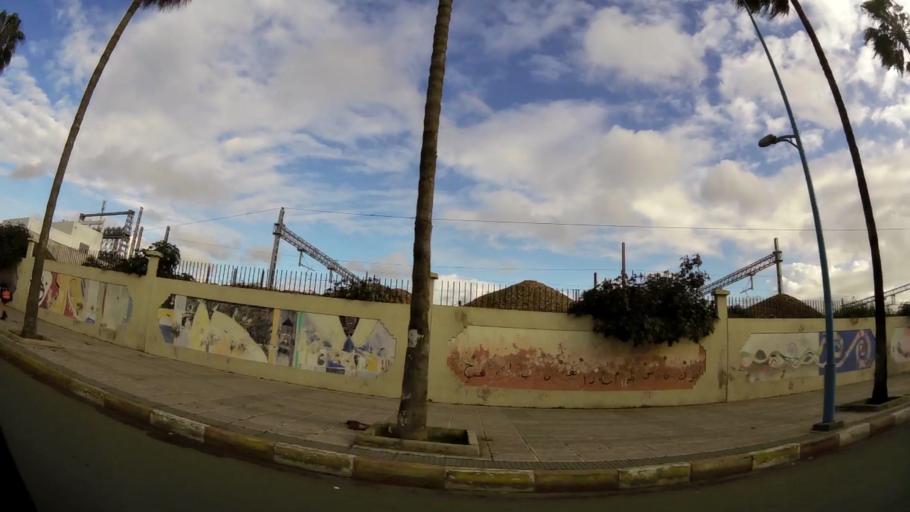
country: MA
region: Grand Casablanca
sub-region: Mohammedia
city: Mohammedia
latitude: 33.6984
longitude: -7.3835
